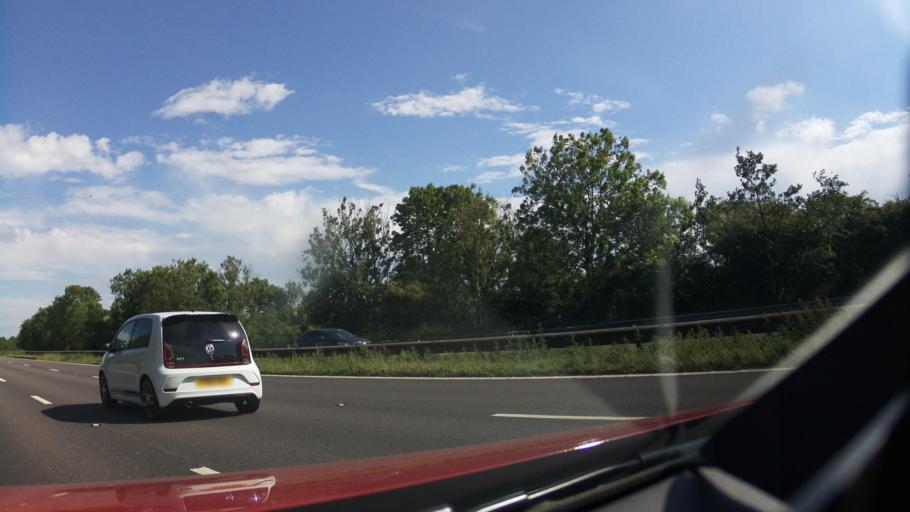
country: GB
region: England
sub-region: Borough of Bolton
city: Blackrod
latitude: 53.5931
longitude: -2.5664
